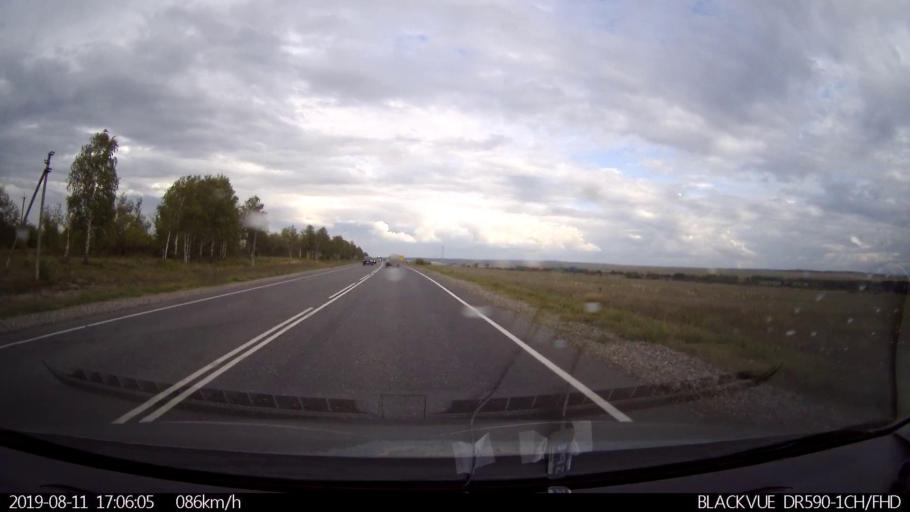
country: RU
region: Ulyanovsk
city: Mayna
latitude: 54.2956
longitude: 47.7990
